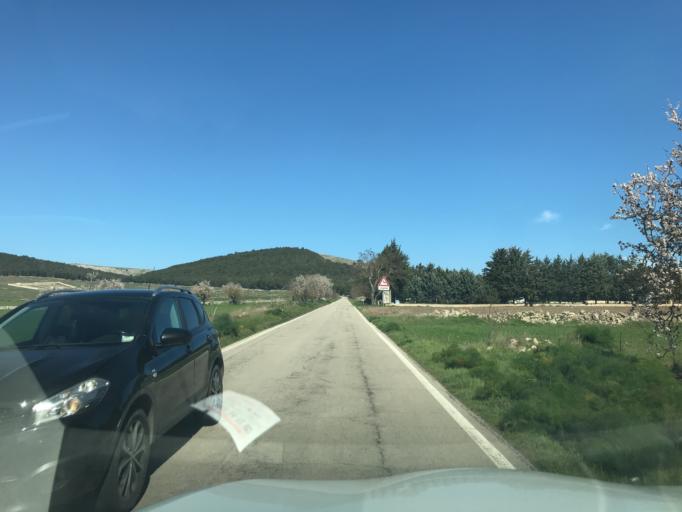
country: IT
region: Apulia
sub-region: Provincia di Bari
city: Gravina in Puglia
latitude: 40.8654
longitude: 16.4398
